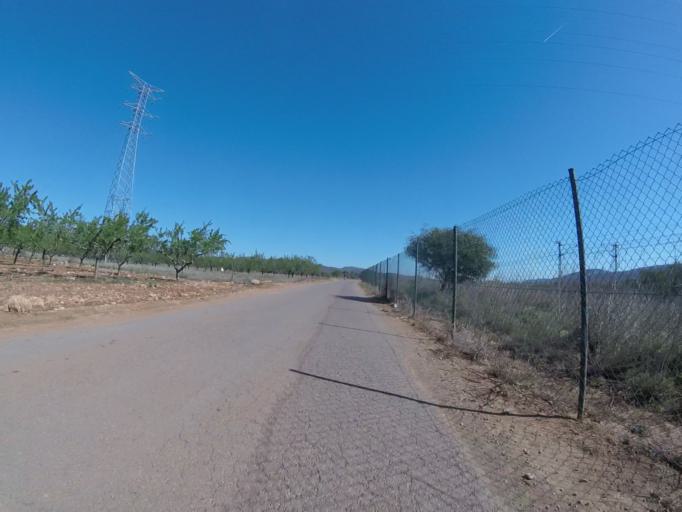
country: ES
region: Valencia
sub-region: Provincia de Castello
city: Alcala de Xivert
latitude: 40.3193
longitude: 0.2347
